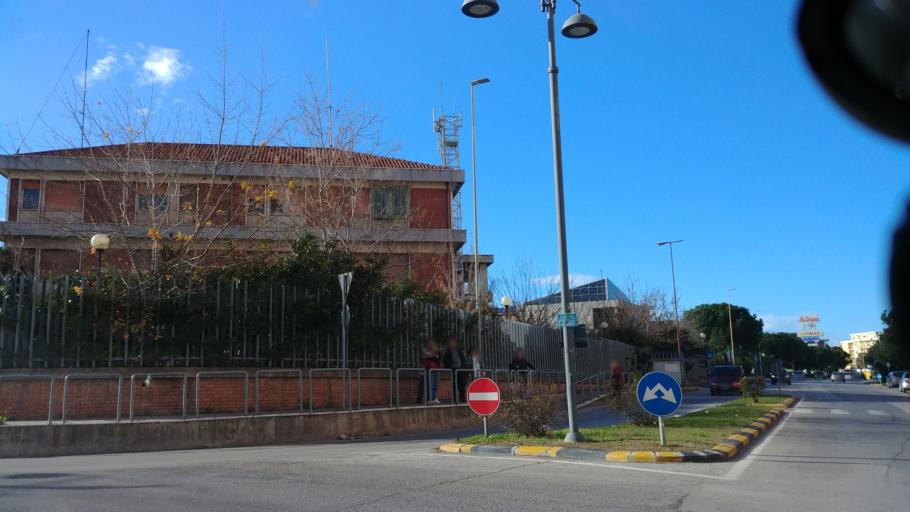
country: IT
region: Molise
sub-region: Provincia di Campobasso
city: Termoli
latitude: 41.9990
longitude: 14.9896
